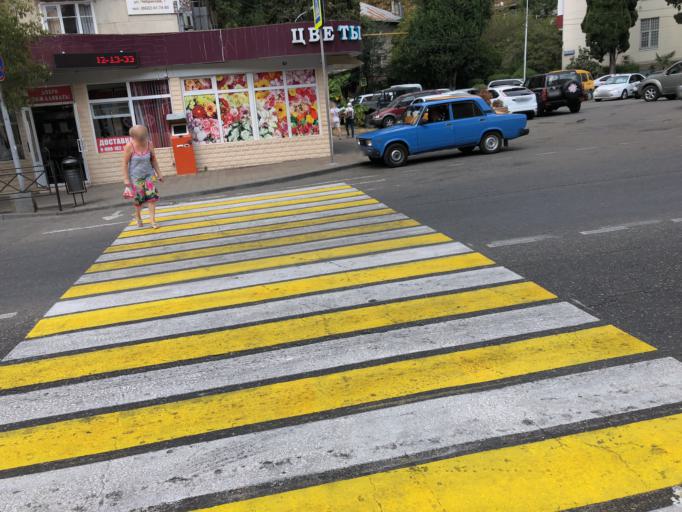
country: RU
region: Krasnodarskiy
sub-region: Sochi City
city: Sochi
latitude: 43.5961
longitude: 39.7340
